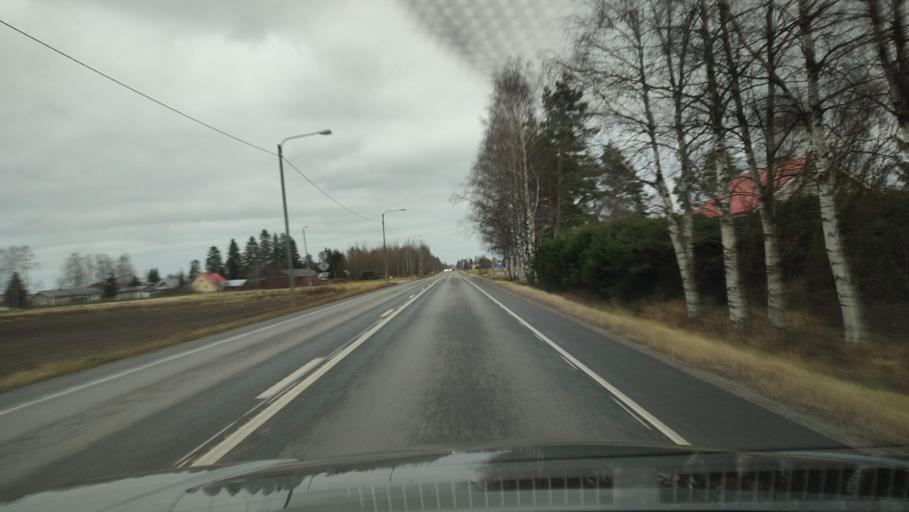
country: FI
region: Southern Ostrobothnia
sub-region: Seinaejoki
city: Ilmajoki
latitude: 62.6937
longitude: 22.4998
